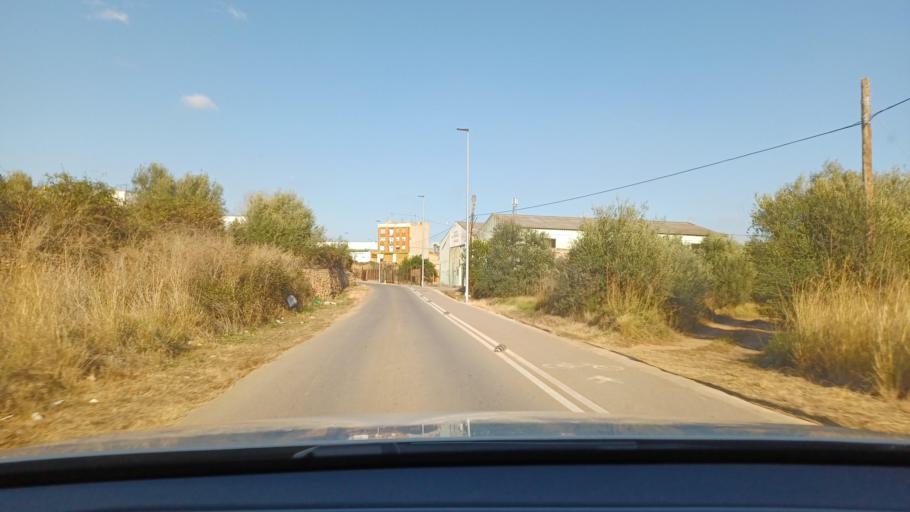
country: ES
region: Valencia
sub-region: Provincia de Castello
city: Onda
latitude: 39.9623
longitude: -0.2530
